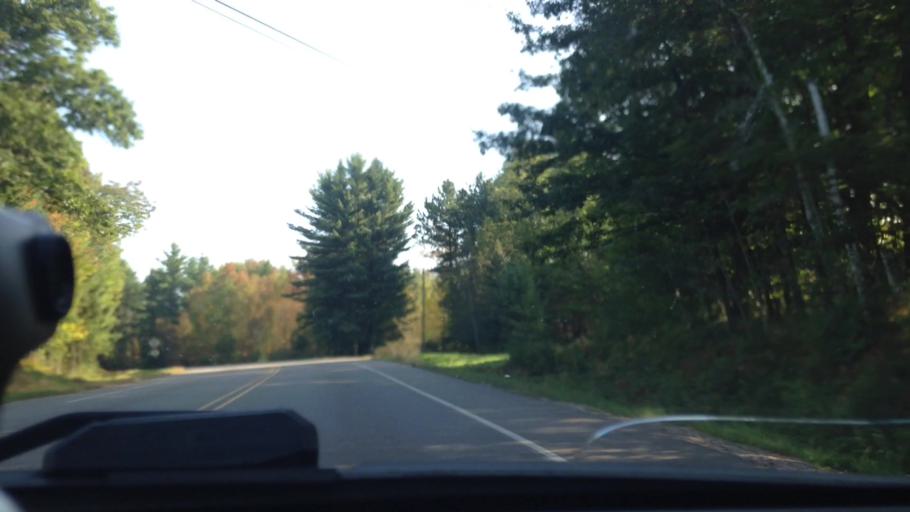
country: US
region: Michigan
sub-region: Dickinson County
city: Quinnesec
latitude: 45.8105
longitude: -87.9868
